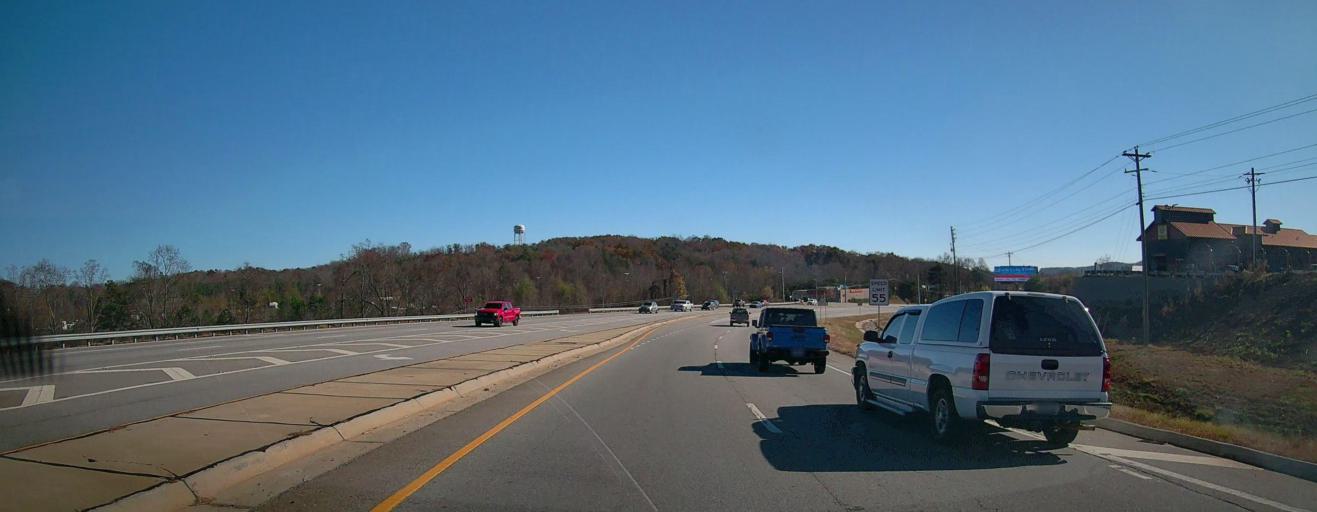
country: US
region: Georgia
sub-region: White County
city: Cleveland
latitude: 34.5789
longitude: -83.7636
